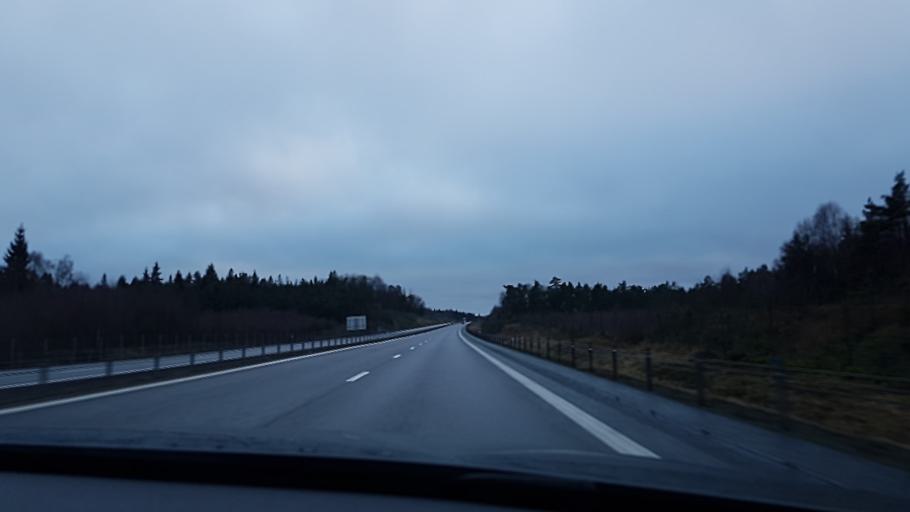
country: SE
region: Kronoberg
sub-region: Markaryds Kommun
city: Markaryd
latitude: 56.3424
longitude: 13.4610
